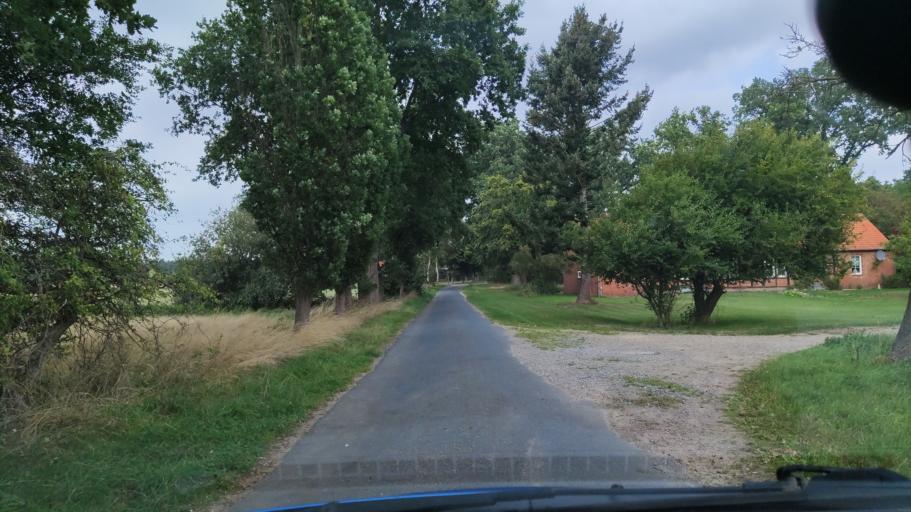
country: DE
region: Lower Saxony
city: Bienenbuttel
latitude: 53.1636
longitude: 10.4997
